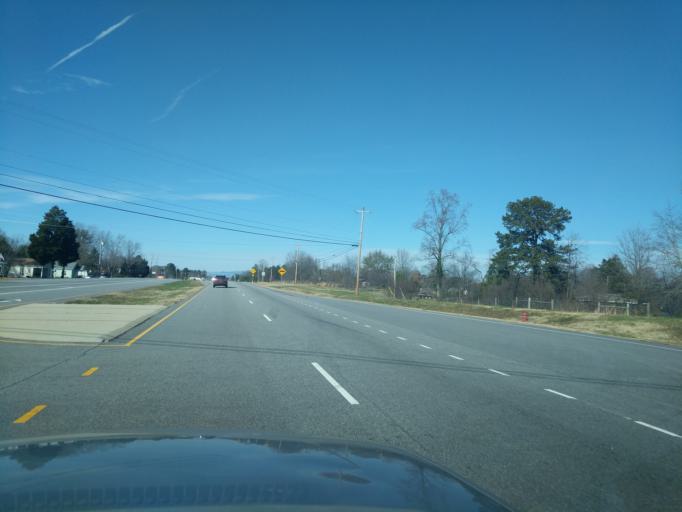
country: US
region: North Carolina
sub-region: Rutherford County
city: Forest City
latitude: 35.2862
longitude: -81.9029
